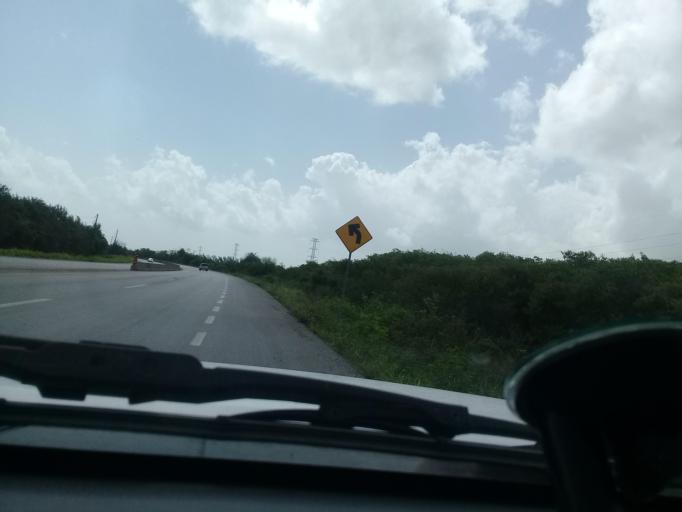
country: MX
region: Veracruz
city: Moralillo
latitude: 22.2119
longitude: -97.9646
